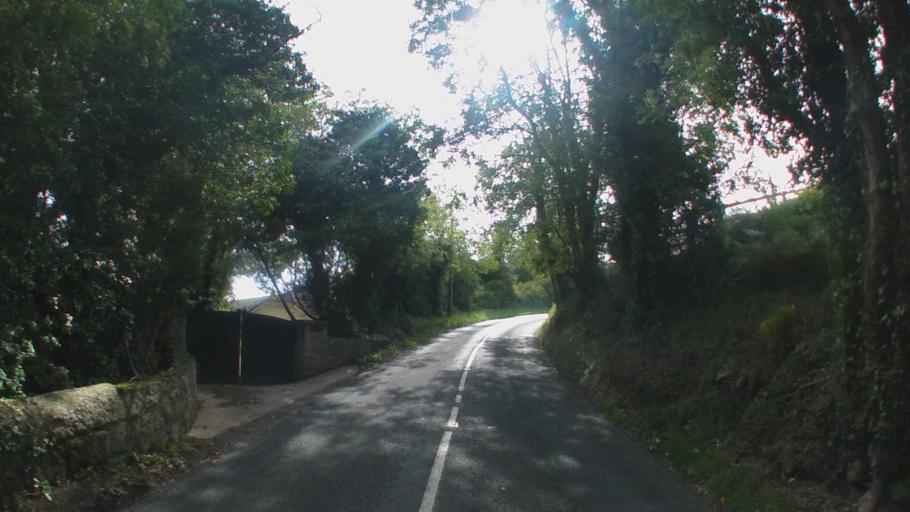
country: IE
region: Leinster
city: Sandyford
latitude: 53.2433
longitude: -6.2215
